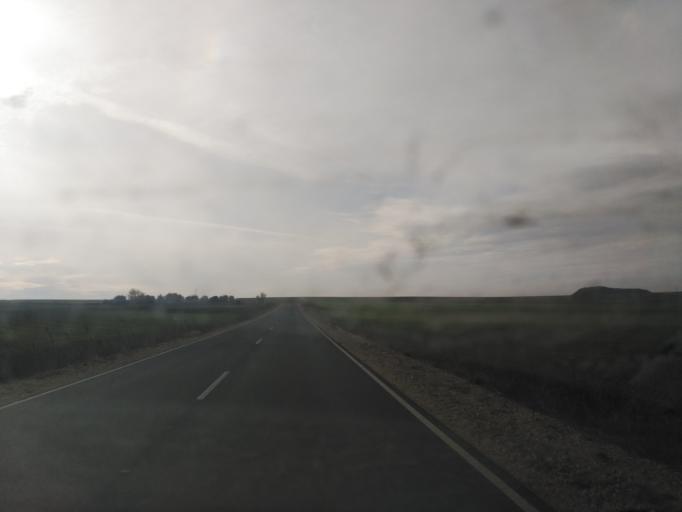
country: ES
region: Castille and Leon
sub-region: Provincia de Salamanca
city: Moriscos
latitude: 41.0041
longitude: -5.5854
